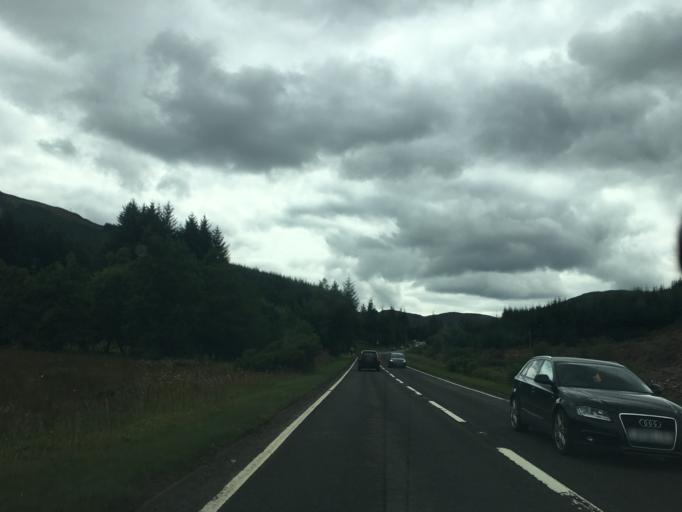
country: GB
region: Scotland
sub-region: Stirling
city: Callander
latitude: 56.4354
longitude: -4.3427
